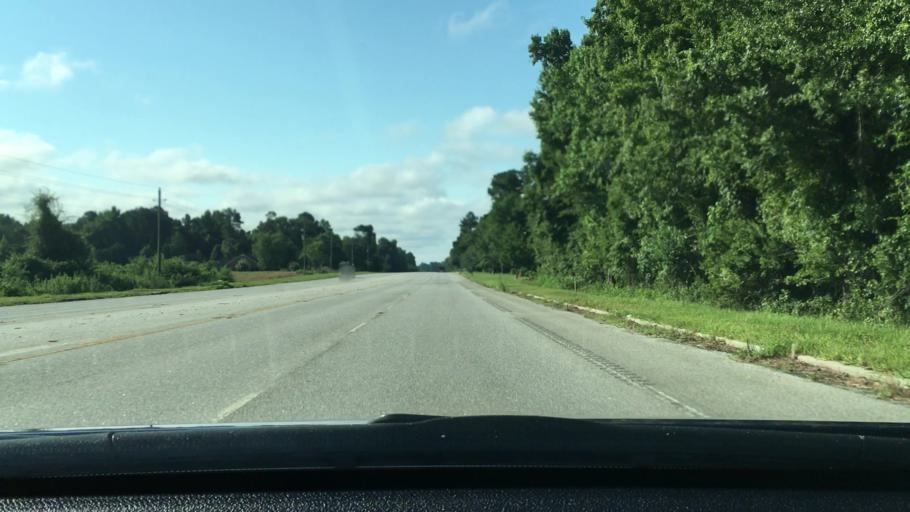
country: US
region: South Carolina
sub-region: Clarendon County
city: Manning
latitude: 33.7607
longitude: -80.2287
